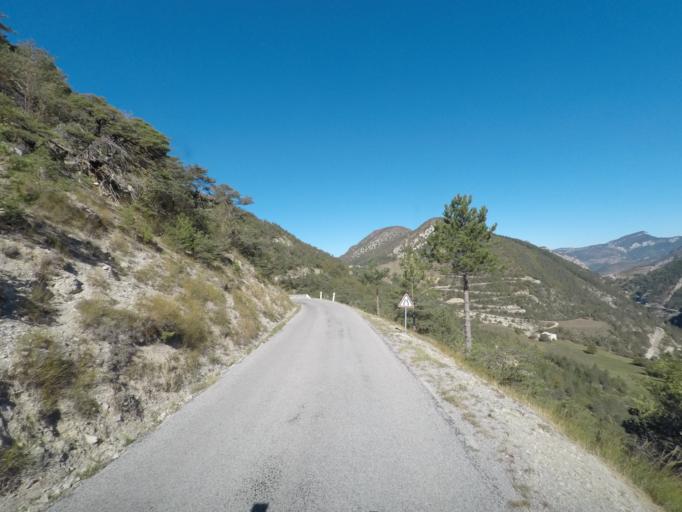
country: FR
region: Rhone-Alpes
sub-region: Departement de la Drome
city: Die
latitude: 44.5683
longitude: 5.3067
